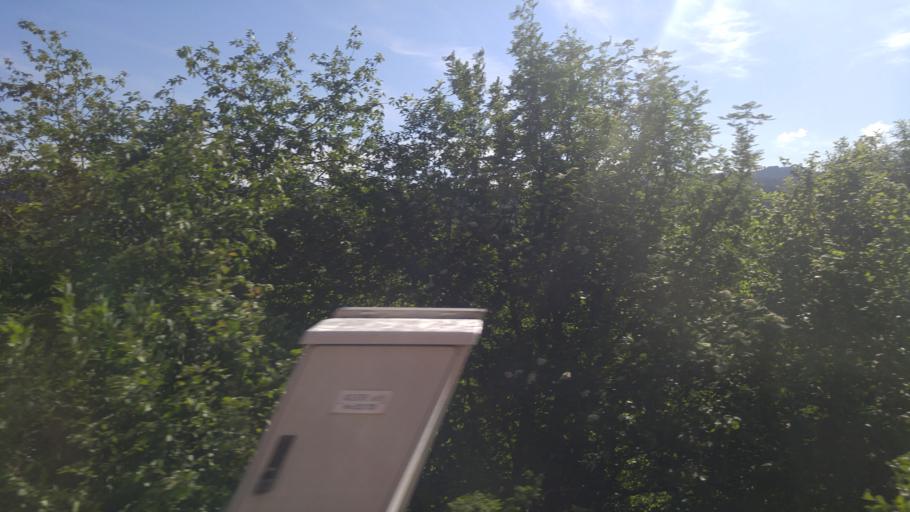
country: NO
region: Sor-Trondelag
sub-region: Melhus
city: Melhus
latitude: 63.2222
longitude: 10.2989
